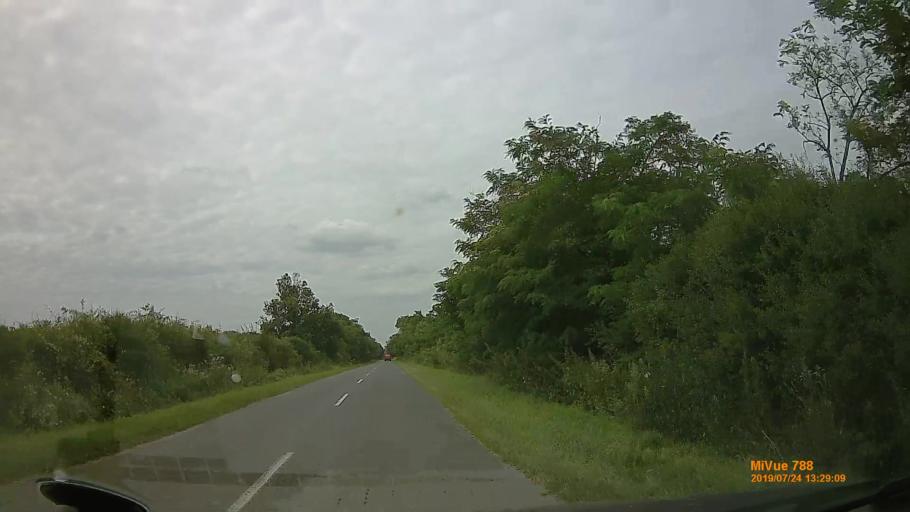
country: HU
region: Szabolcs-Szatmar-Bereg
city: Vasarosnameny
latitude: 48.2254
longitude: 22.4044
